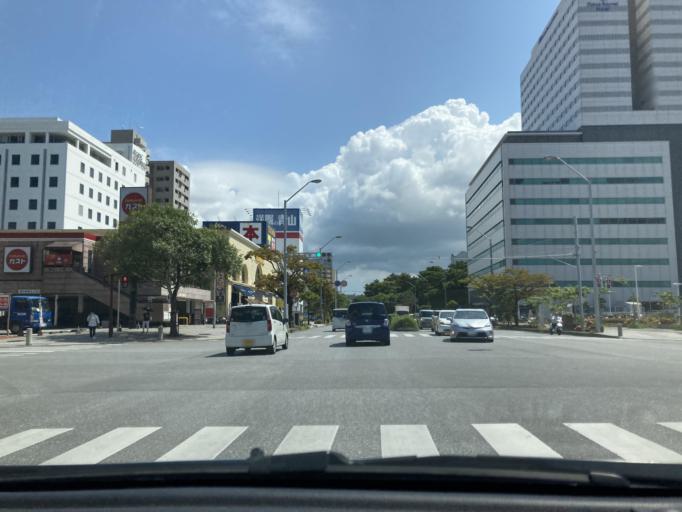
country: JP
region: Okinawa
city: Naha-shi
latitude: 26.2244
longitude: 127.6949
